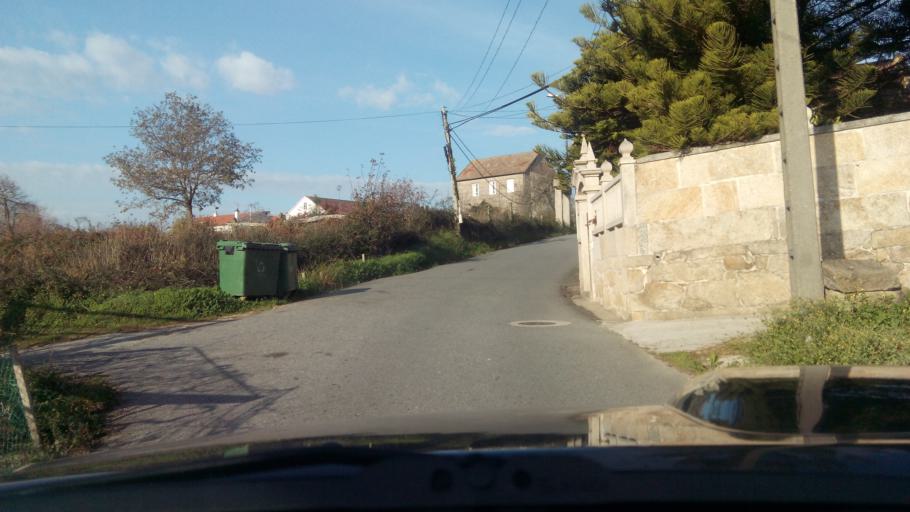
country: ES
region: Galicia
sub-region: Provincia de Pontevedra
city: Marin
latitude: 42.3688
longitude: -8.7286
